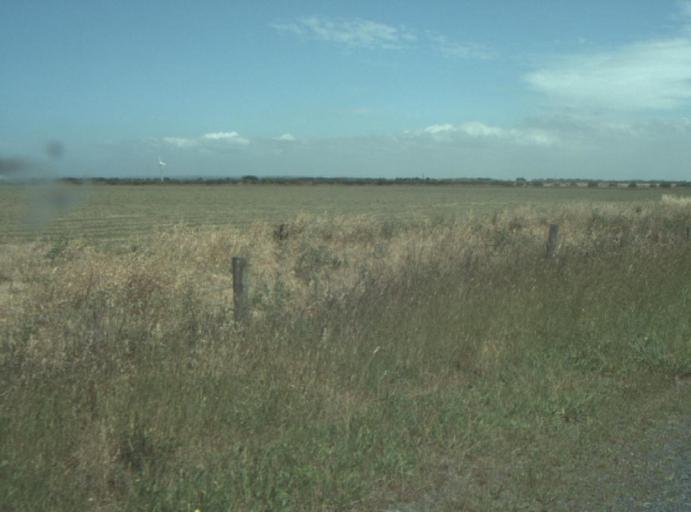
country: AU
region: Victoria
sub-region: Greater Geelong
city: Leopold
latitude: -38.2759
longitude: 144.4315
